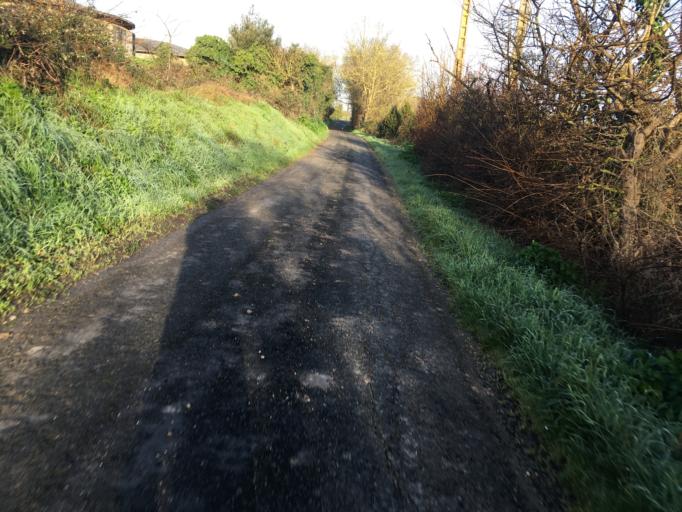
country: FR
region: Poitou-Charentes
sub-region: Departement de la Charente-Maritime
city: Nieul-sur-Mer
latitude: 46.1984
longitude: -1.1795
